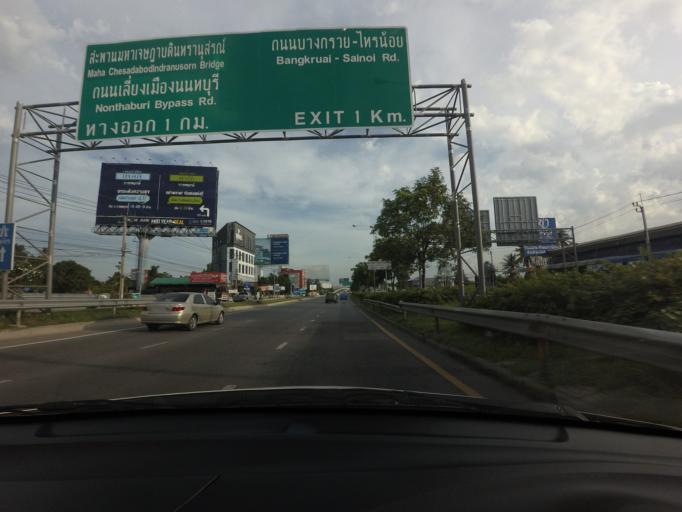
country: TH
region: Nonthaburi
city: Bang Bua Thong
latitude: 13.8617
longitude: 100.4515
